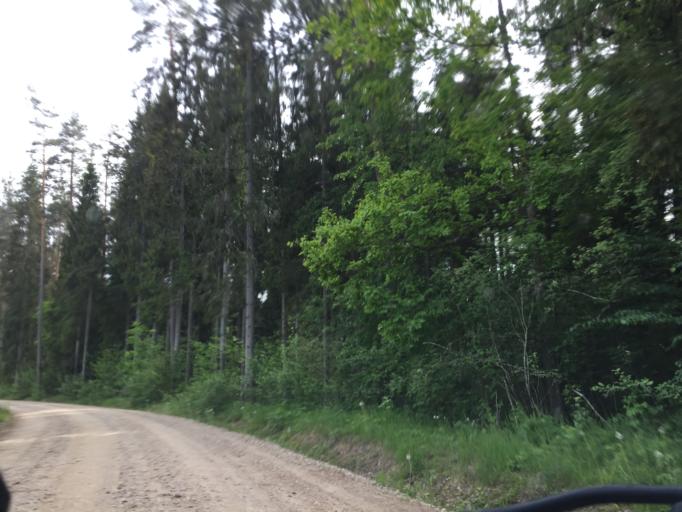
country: LV
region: Valmieras Rajons
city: Valmiera
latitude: 57.4750
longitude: 25.3987
